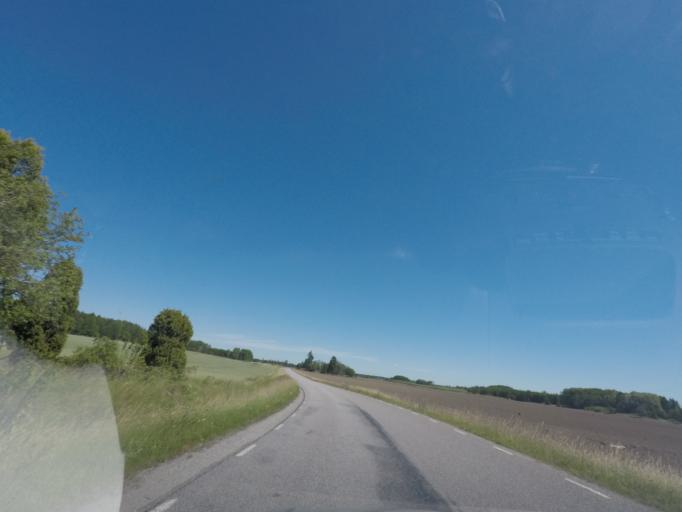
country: SE
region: Uppsala
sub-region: Enkopings Kommun
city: Irsta
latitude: 59.6762
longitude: 16.9433
